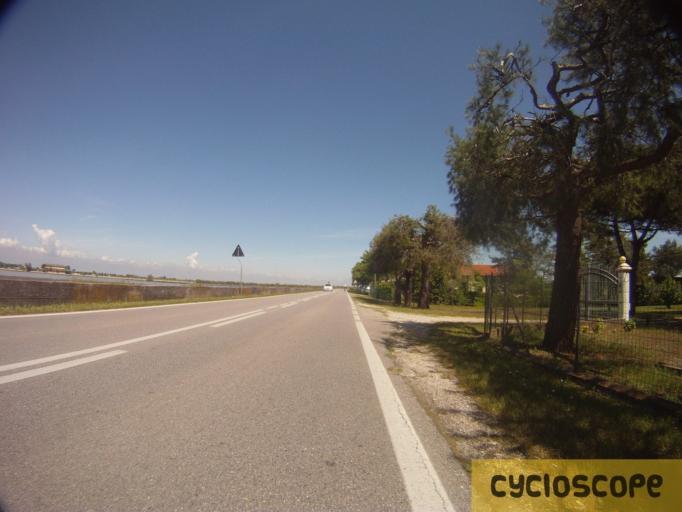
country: IT
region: Veneto
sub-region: Provincia di Venezia
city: Ca' Savio
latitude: 45.4704
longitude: 12.4972
